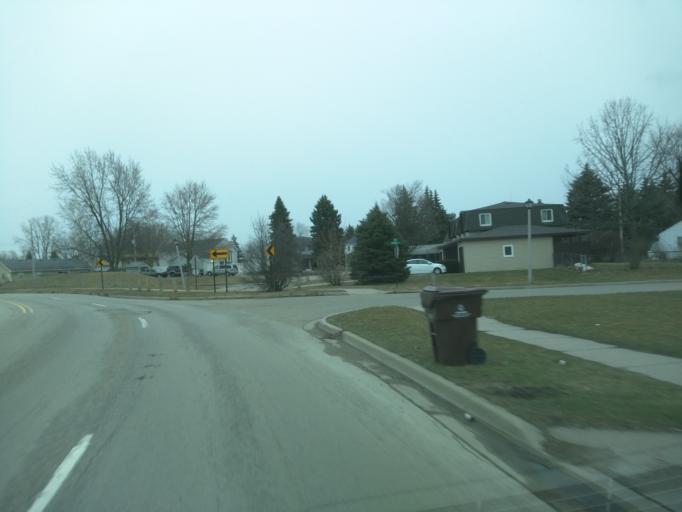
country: US
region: Michigan
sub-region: Eaton County
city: Waverly
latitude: 42.7369
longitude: -84.6219
